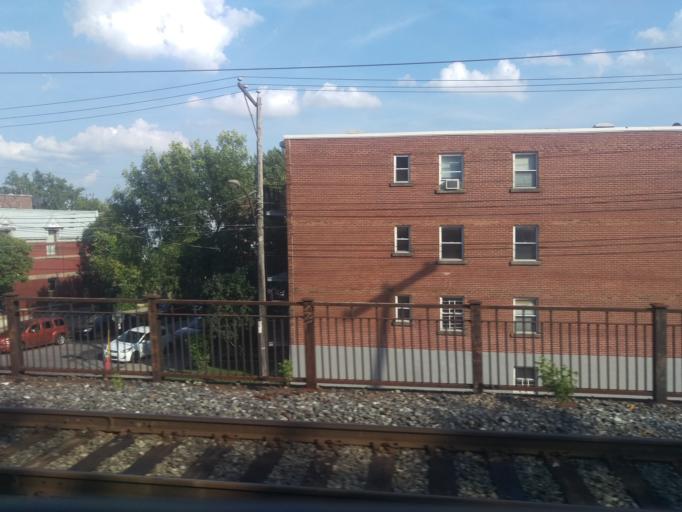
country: CA
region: Quebec
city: Westmount
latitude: 45.4792
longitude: -73.5626
